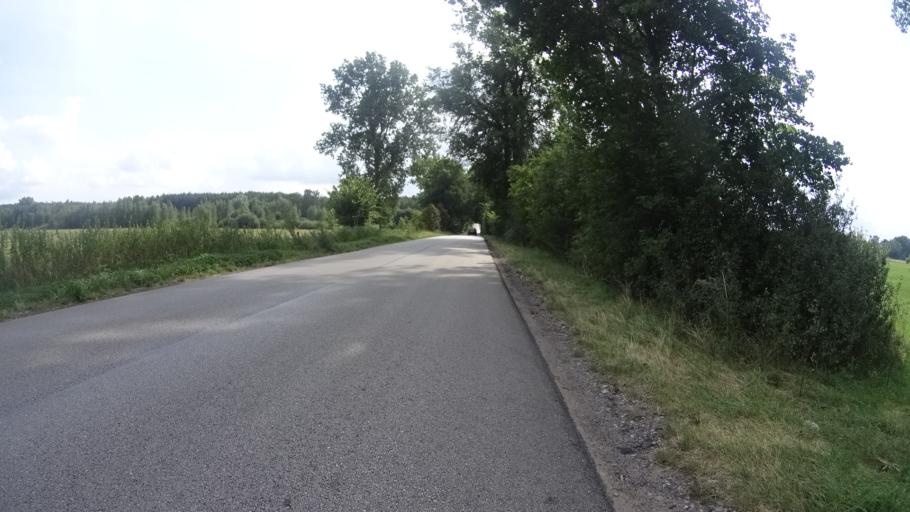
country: PL
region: Masovian Voivodeship
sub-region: Powiat bialobrzeski
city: Wysmierzyce
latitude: 51.6544
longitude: 20.7725
